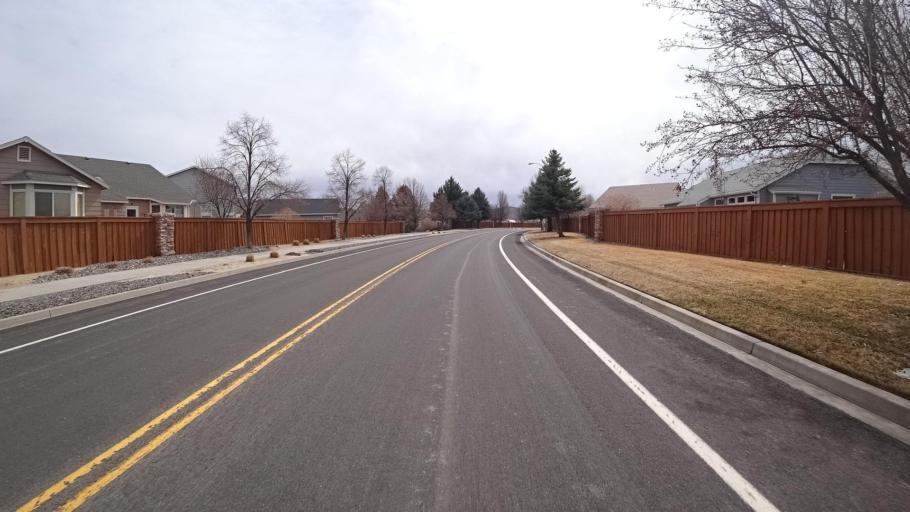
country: US
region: Nevada
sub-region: Washoe County
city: Spanish Springs
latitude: 39.6305
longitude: -119.6852
